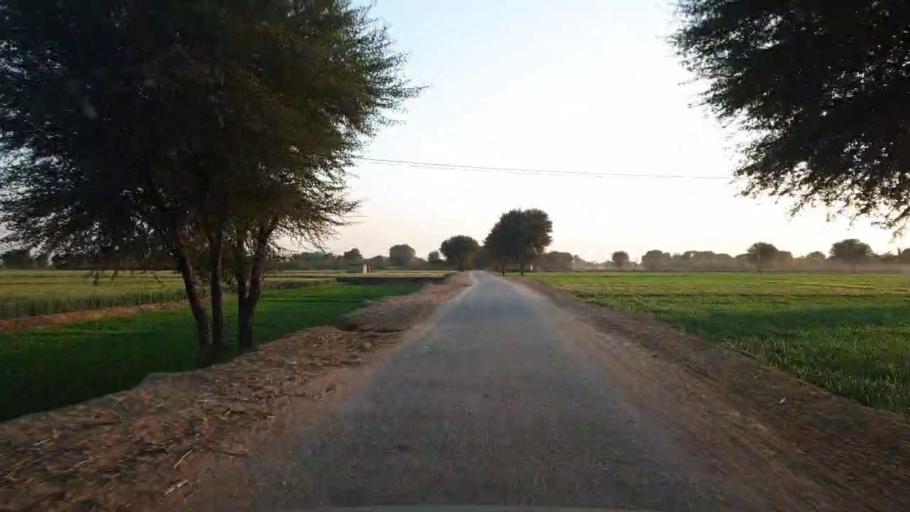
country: PK
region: Sindh
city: Tando Jam
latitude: 25.3059
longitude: 68.6382
